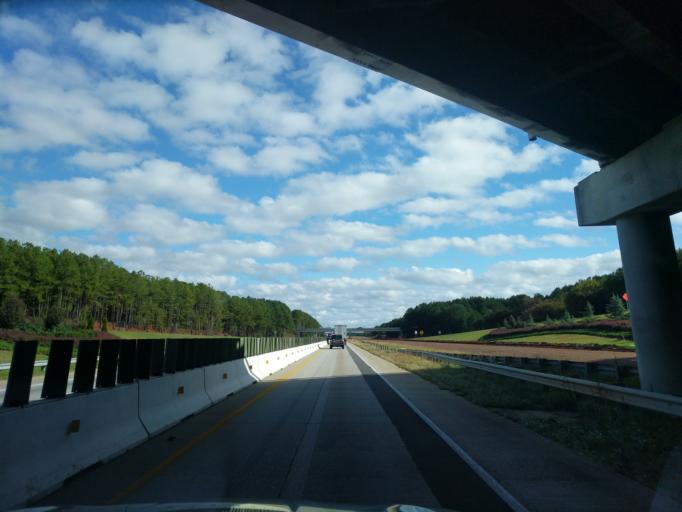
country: US
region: South Carolina
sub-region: Spartanburg County
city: Southern Shops
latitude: 34.9962
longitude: -81.9938
